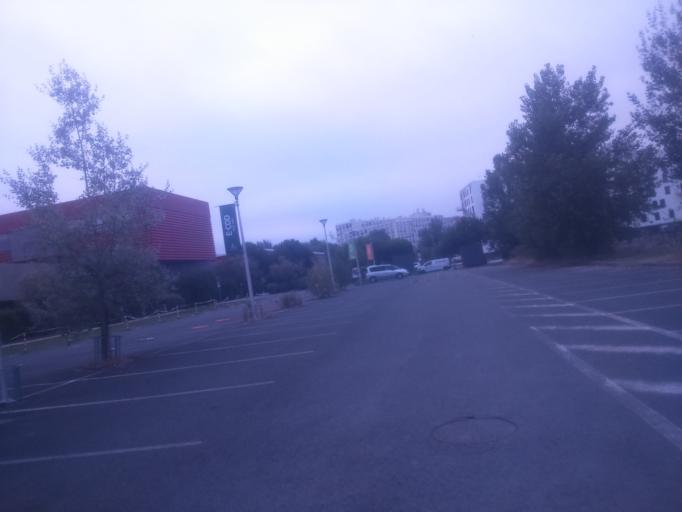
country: FR
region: Aquitaine
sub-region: Departement de la Gironde
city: Le Bouscat
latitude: 44.8769
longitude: -0.5748
